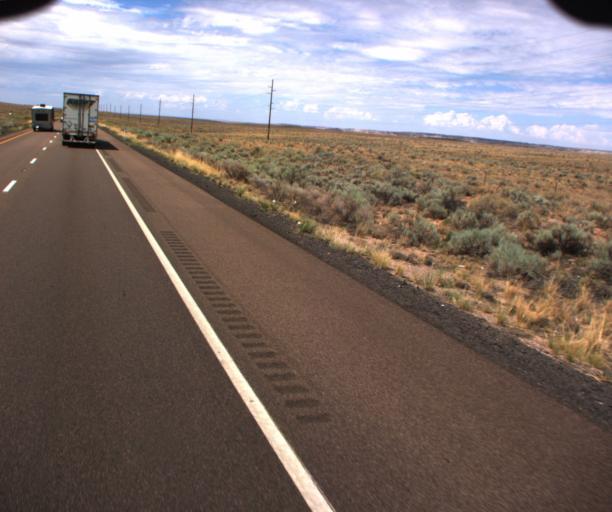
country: US
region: Arizona
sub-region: Navajo County
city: Holbrook
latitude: 35.0334
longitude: -109.8287
